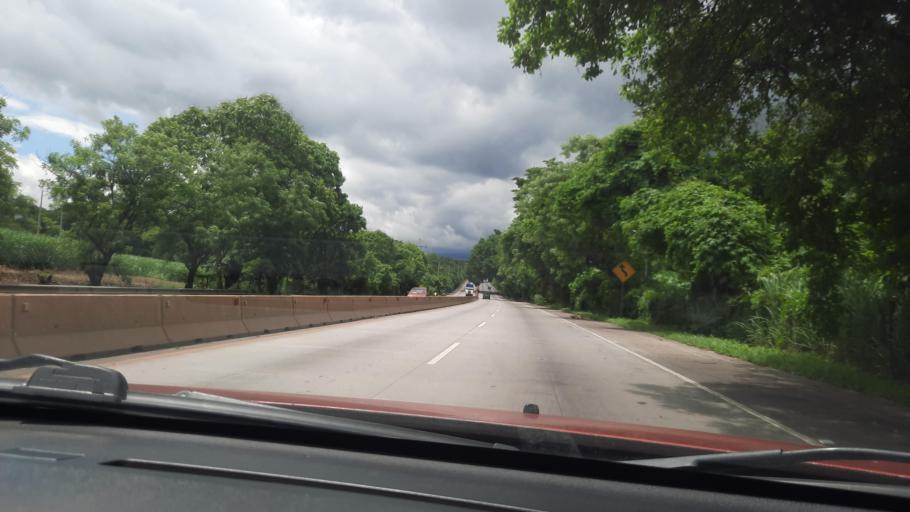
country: SV
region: Sonsonate
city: Sonzacate
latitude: 13.7290
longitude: -89.7020
